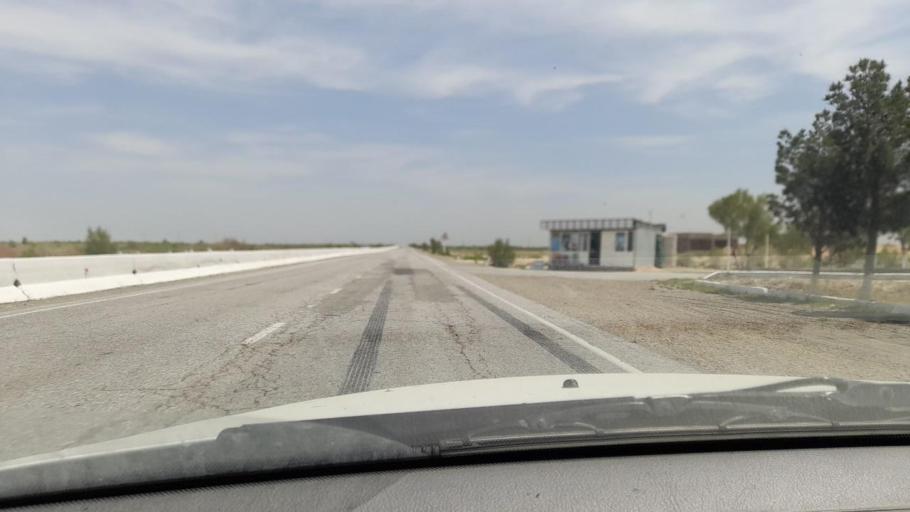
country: UZ
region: Navoiy
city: Qiziltepa
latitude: 40.0844
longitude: 64.9467
